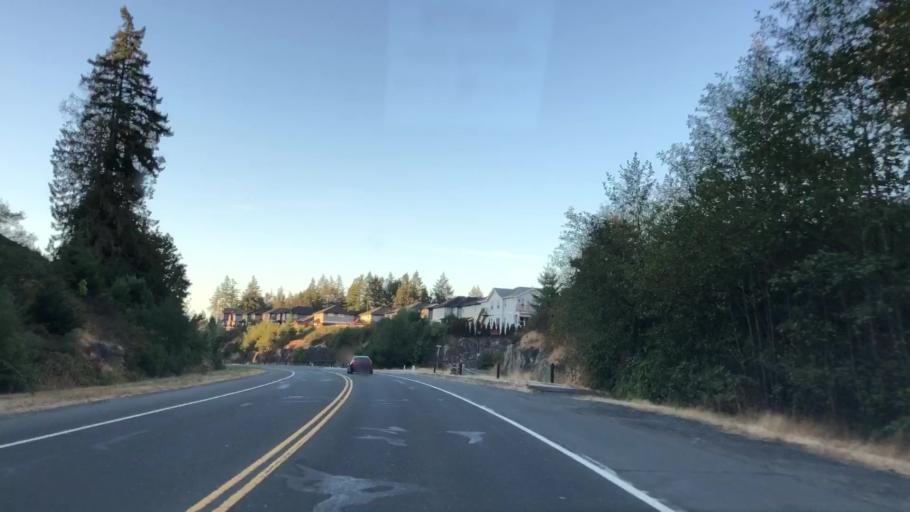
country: CA
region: British Columbia
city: Colwood
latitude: 48.4191
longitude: -123.5055
